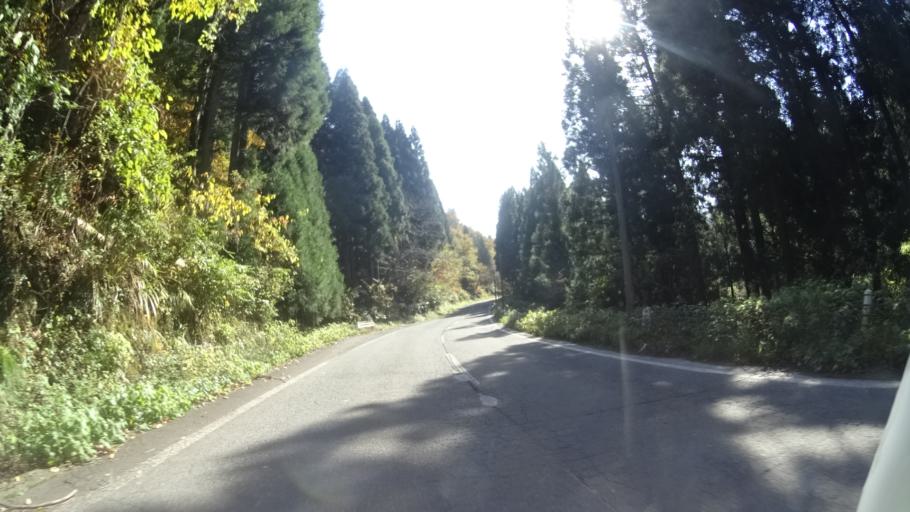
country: JP
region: Fukui
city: Ono
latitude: 35.8692
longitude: 136.3620
